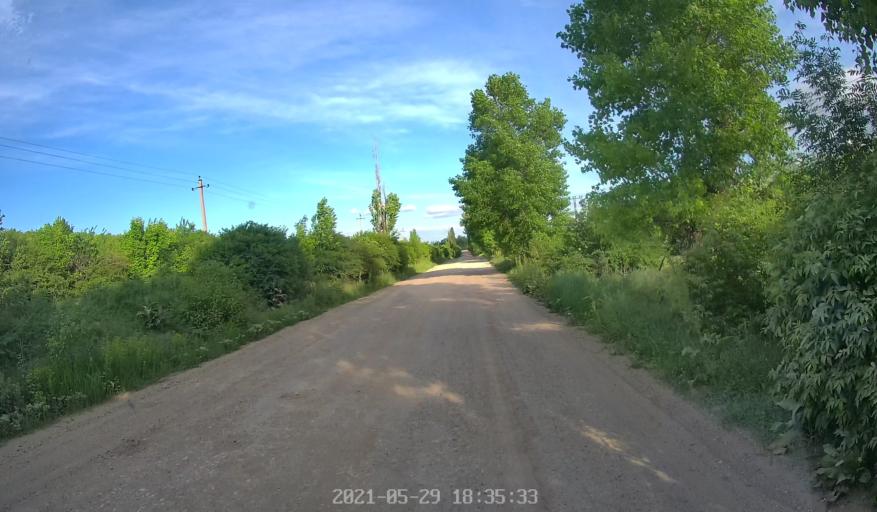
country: MD
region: Chisinau
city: Singera
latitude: 46.8090
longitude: 28.9201
